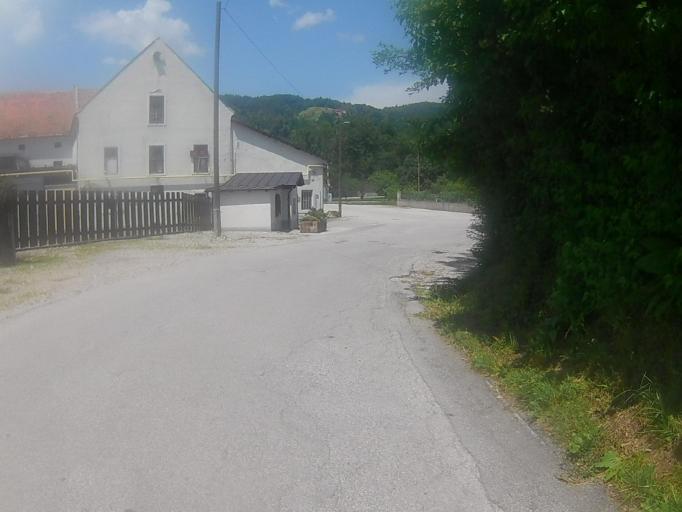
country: SI
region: Ruse
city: Bistrica ob Dravi
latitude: 46.5560
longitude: 15.5498
